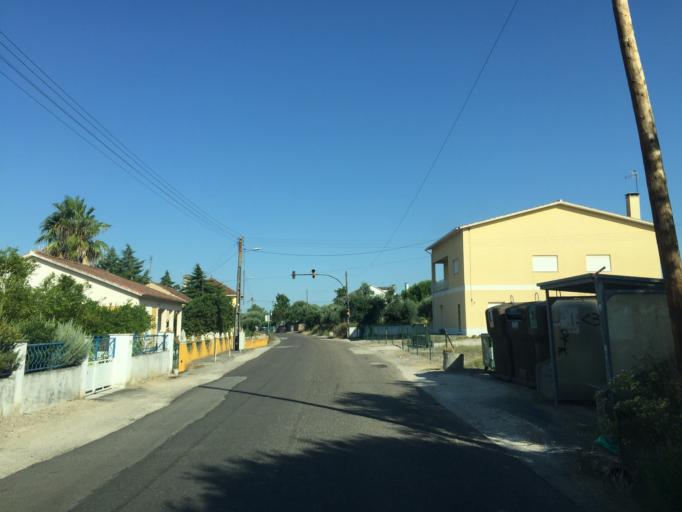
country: PT
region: Santarem
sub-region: Tomar
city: Tomar
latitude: 39.5968
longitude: -8.3777
